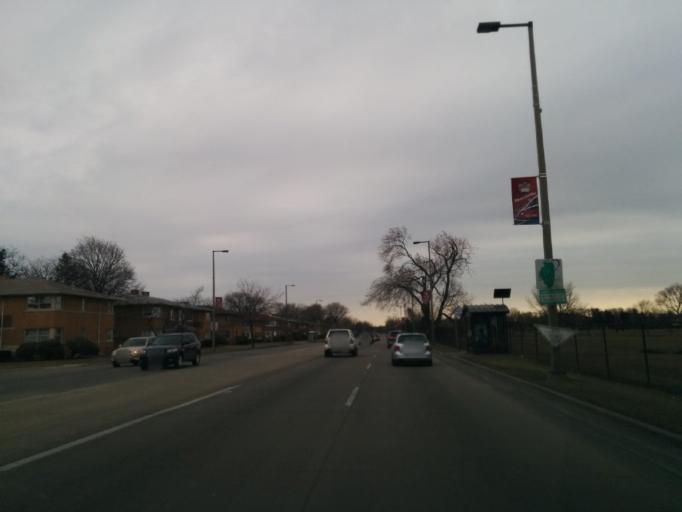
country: US
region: Illinois
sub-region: Cook County
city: Westchester
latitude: 41.8609
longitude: -87.8824
